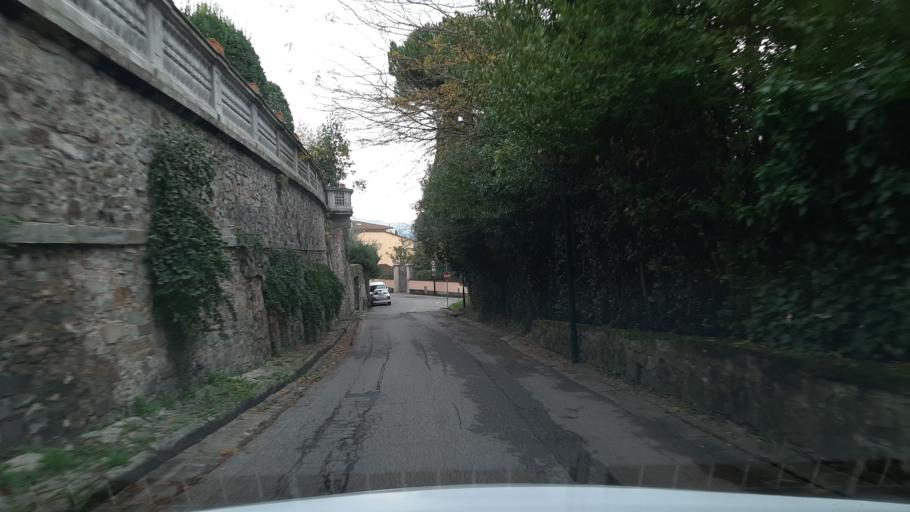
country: IT
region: Tuscany
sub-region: Province of Florence
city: Fiesole
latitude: 43.7831
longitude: 11.2970
